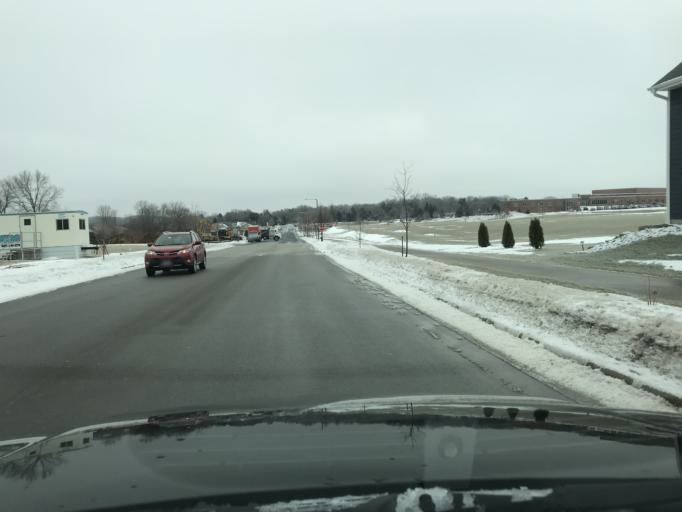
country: US
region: Wisconsin
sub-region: Dane County
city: Cottage Grove
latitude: 43.0940
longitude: -89.2203
